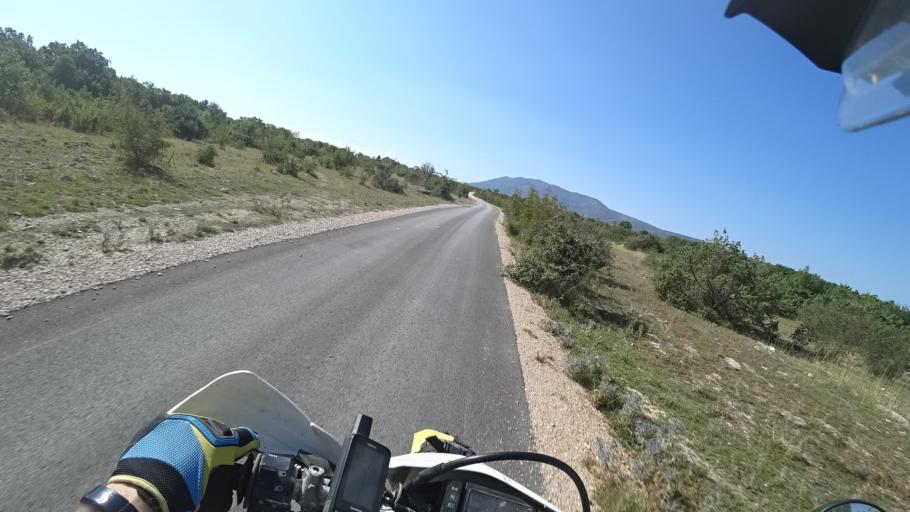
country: HR
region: Sibensko-Kniniska
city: Knin
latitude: 44.0005
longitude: 16.1939
